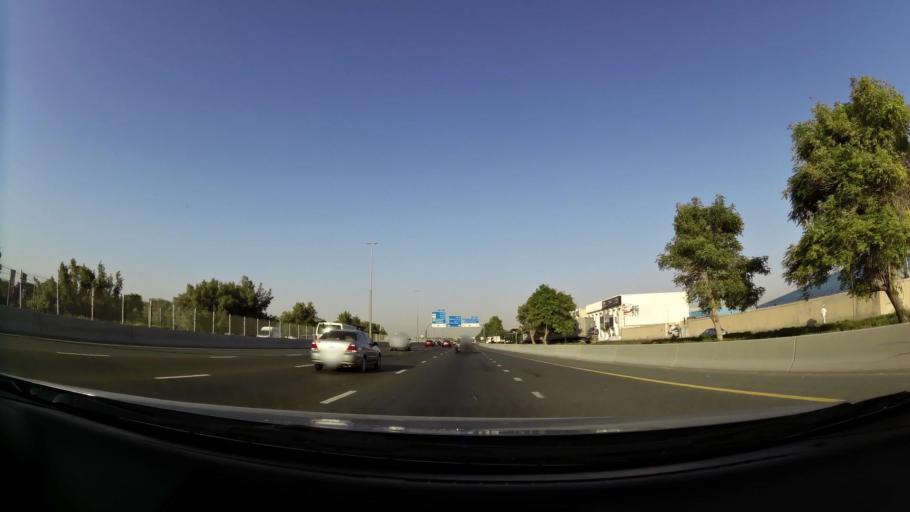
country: AE
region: Ash Shariqah
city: Sharjah
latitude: 25.1856
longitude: 55.3576
